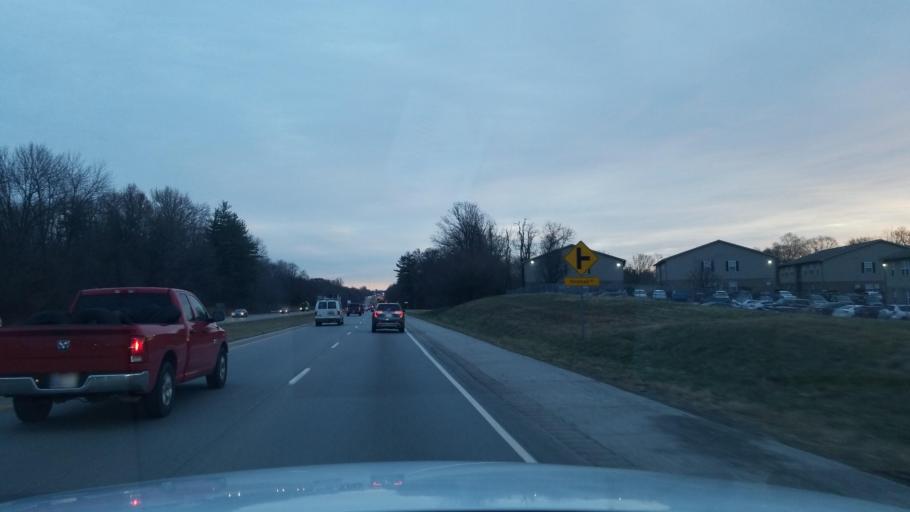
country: US
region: Indiana
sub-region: Vanderburgh County
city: Evansville
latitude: 37.9699
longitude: -87.6634
